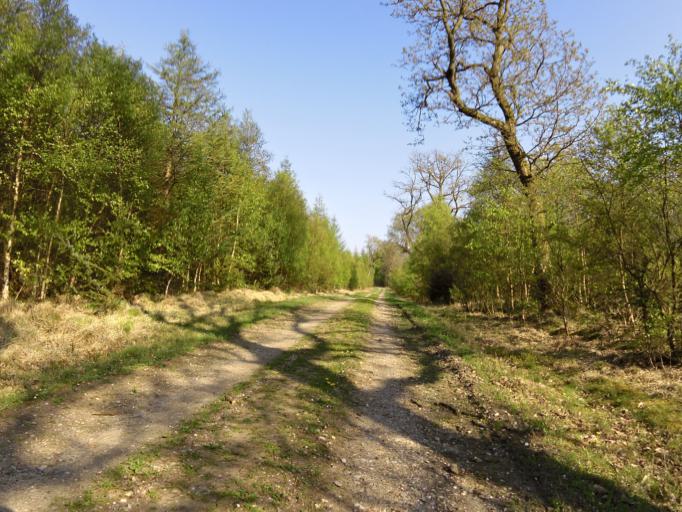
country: DK
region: South Denmark
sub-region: Tonder Kommune
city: Toftlund
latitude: 55.1948
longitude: 8.9455
